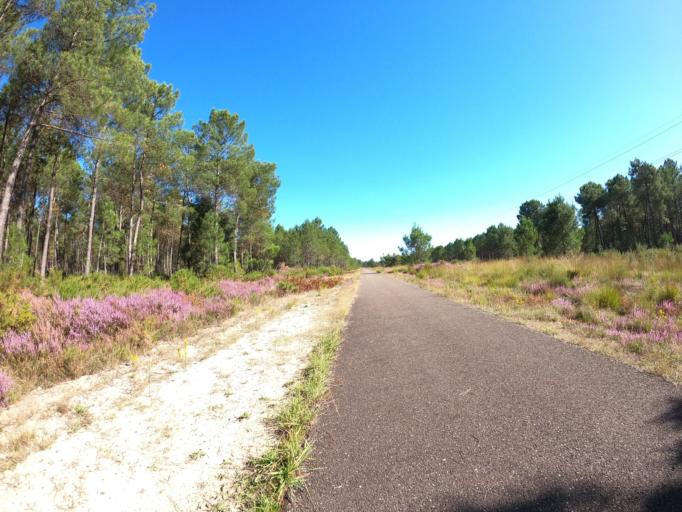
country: FR
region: Aquitaine
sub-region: Departement des Landes
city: Ychoux
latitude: 44.3391
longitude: -0.9612
